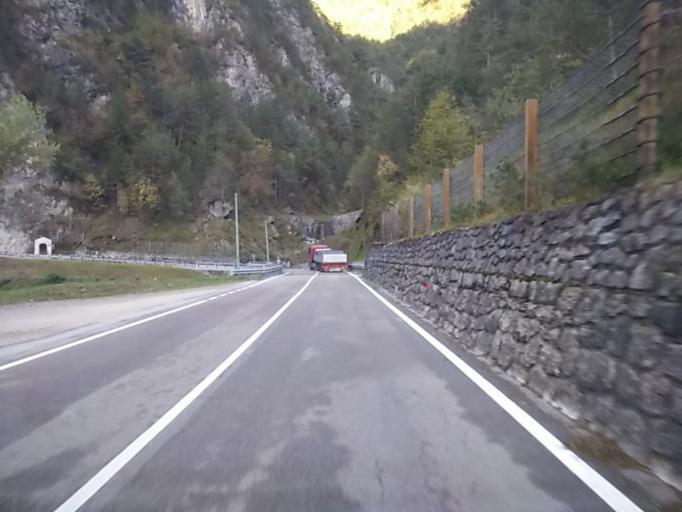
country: IT
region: Trentino-Alto Adige
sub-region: Provincia di Trento
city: Storo
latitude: 45.8406
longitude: 10.5944
